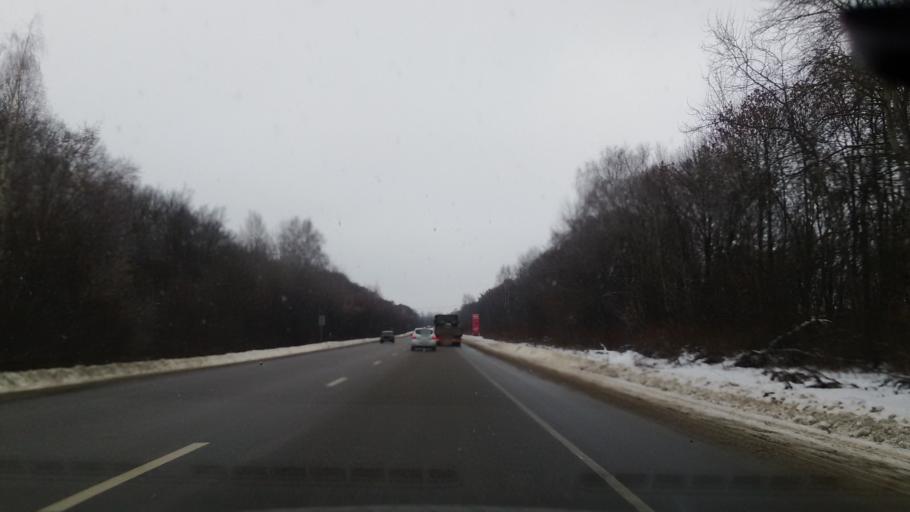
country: RU
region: Tula
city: Kireyevsk
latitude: 54.0198
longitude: 37.9196
